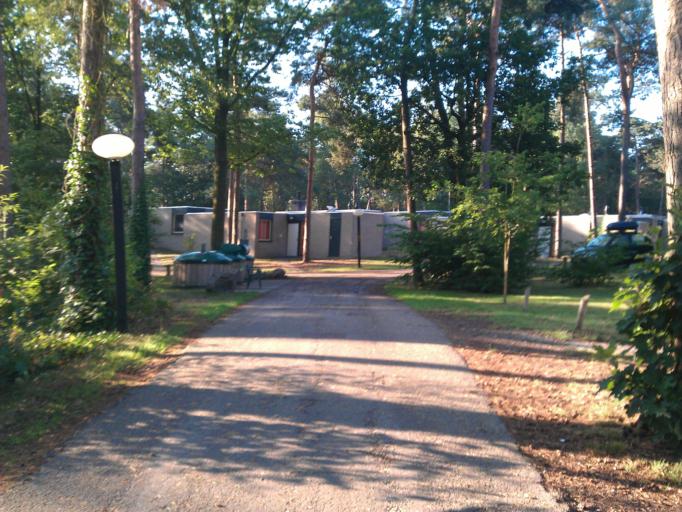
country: NL
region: North Brabant
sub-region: Gemeente Bladel en Netersel
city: Bladel
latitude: 51.3422
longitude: 5.2548
